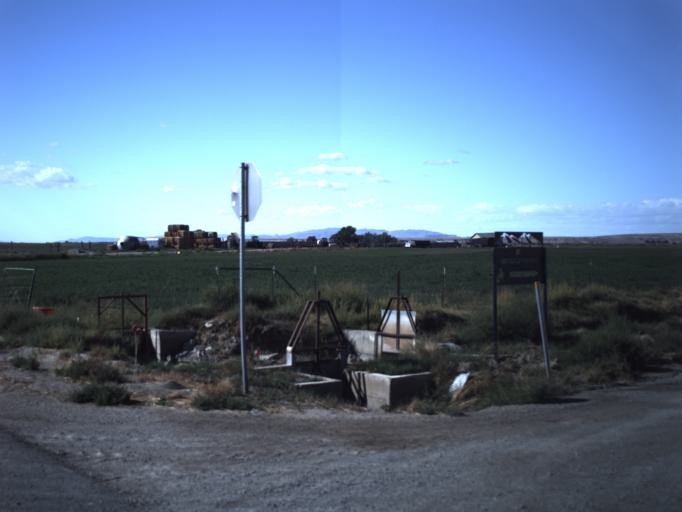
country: US
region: Utah
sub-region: Millard County
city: Delta
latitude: 39.2724
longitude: -112.6531
